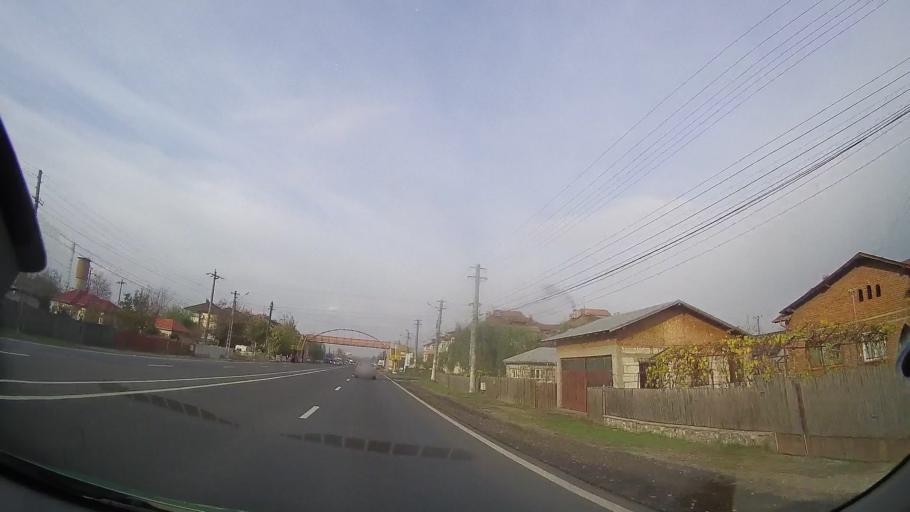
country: RO
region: Prahova
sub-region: Comuna Puchenii Mari
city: Miroslavesti
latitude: 44.8029
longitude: 26.0852
